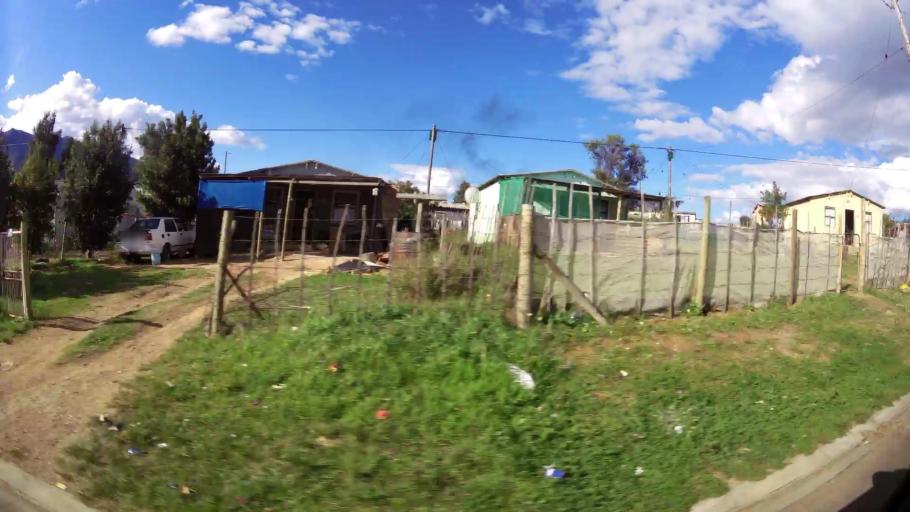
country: ZA
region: Western Cape
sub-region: Overberg District Municipality
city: Swellendam
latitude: -34.0345
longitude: 20.4517
